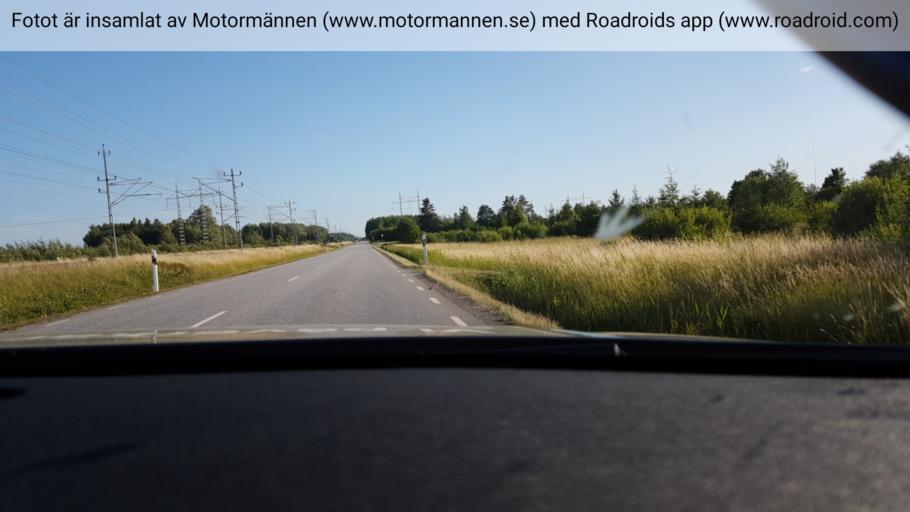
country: SE
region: Vaestra Goetaland
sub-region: Toreboda Kommun
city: Toereboda
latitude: 58.6884
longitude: 14.1122
